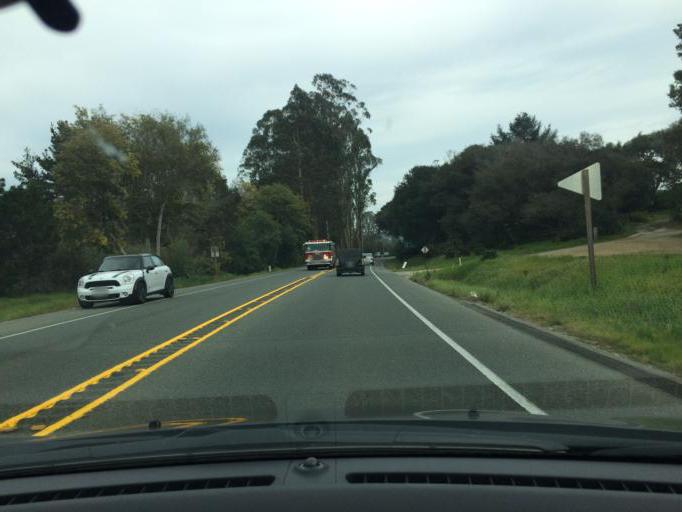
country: US
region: California
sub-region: Monterey County
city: Prunedale
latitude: 36.7874
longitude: -121.6822
